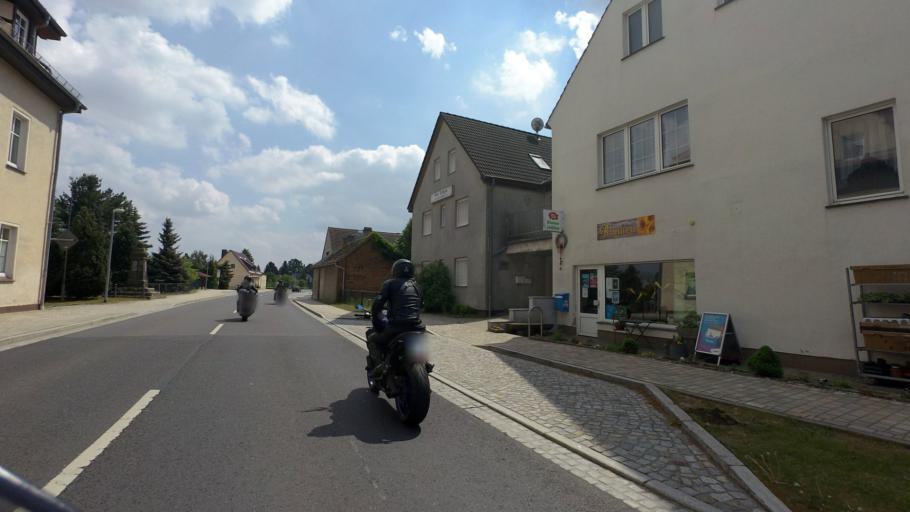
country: DE
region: Saxony
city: Weisskeissel
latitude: 51.4940
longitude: 14.7200
